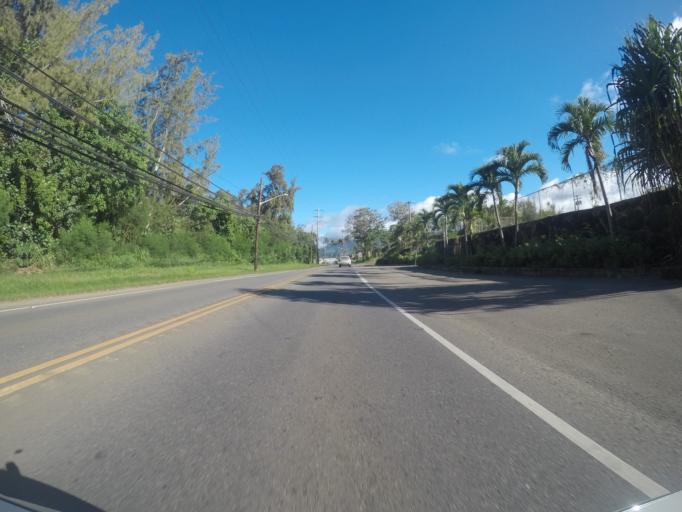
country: US
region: Hawaii
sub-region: Honolulu County
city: La'ie
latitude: 21.6563
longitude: -157.9307
